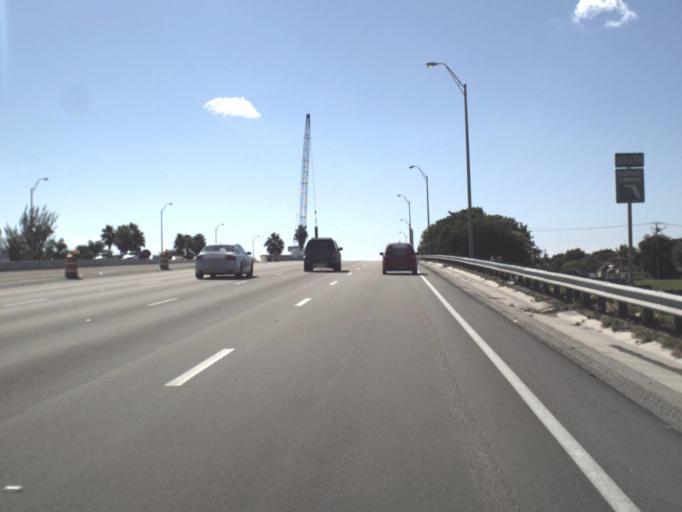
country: US
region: Florida
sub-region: Miami-Dade County
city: South Miami Heights
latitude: 25.6148
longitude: -80.3788
